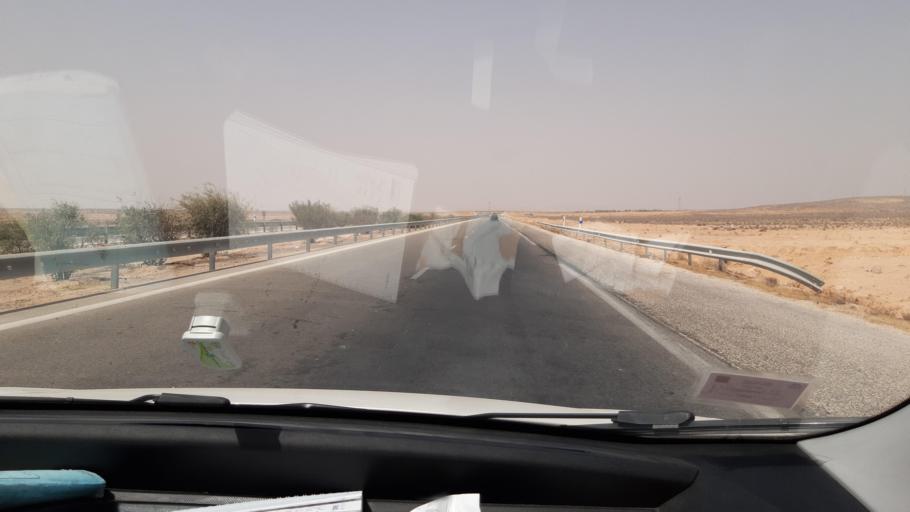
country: TN
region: Qabis
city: Gabes
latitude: 33.9013
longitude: 9.9796
